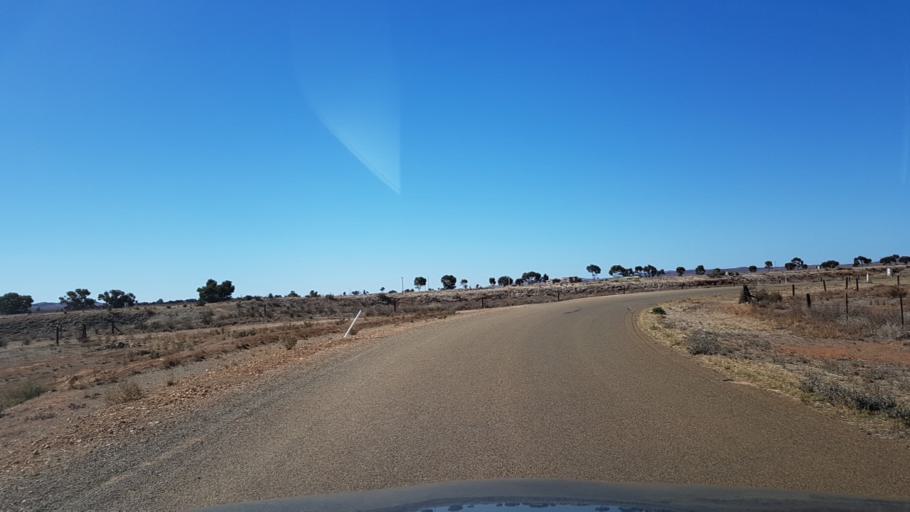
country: AU
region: South Australia
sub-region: Peterborough
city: Peterborough
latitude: -32.9733
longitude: 138.8541
